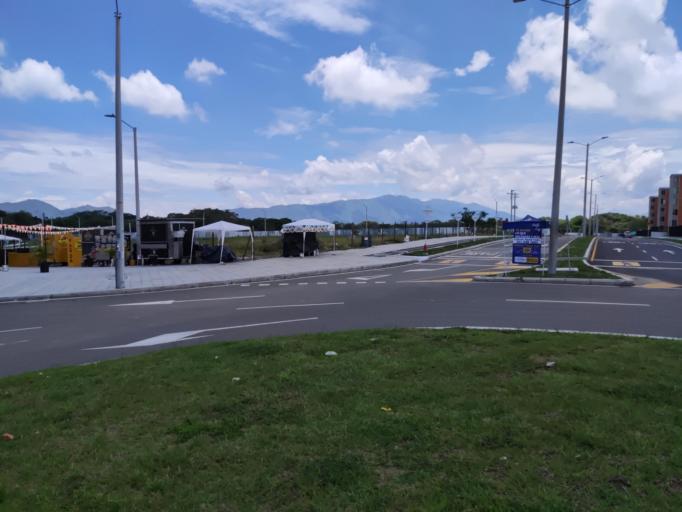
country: CO
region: Tolima
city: Ibague
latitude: 4.3897
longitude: -75.1401
